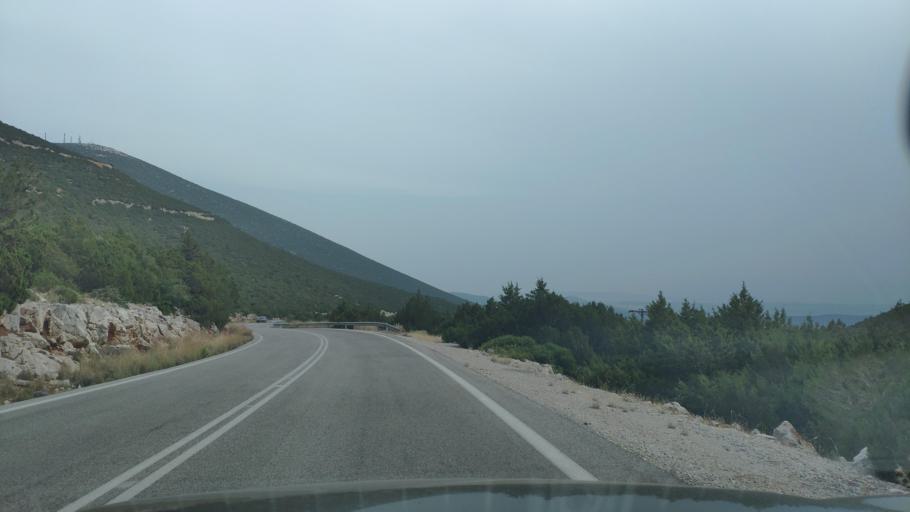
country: GR
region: Peloponnese
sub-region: Nomos Argolidos
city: Didyma
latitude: 37.4988
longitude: 23.1909
